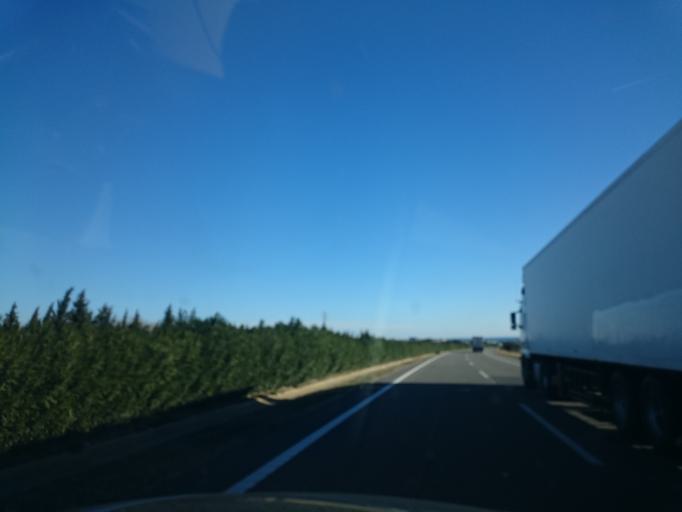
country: ES
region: Catalonia
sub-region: Provincia de Tarragona
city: Camarles
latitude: 40.8020
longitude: 0.6782
